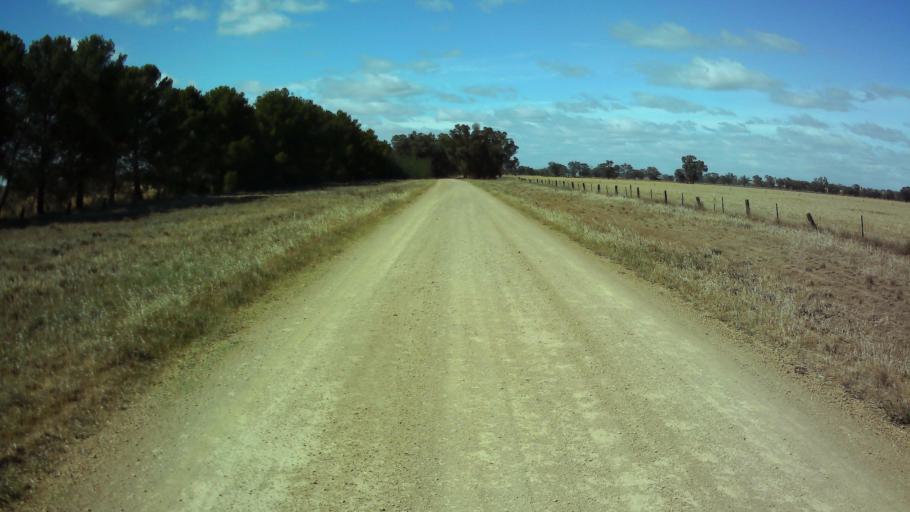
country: AU
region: New South Wales
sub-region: Weddin
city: Grenfell
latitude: -34.0339
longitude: 148.3169
